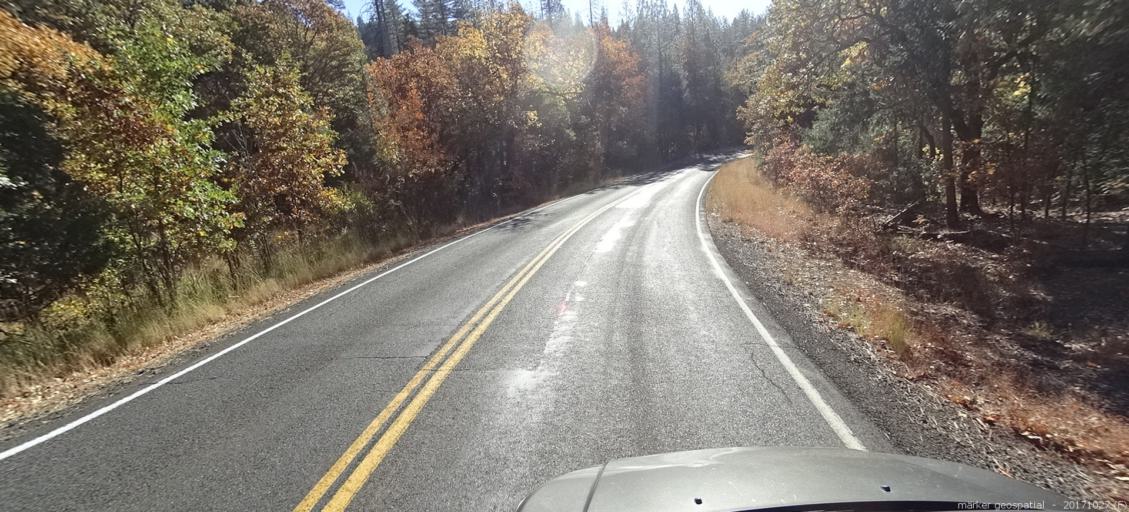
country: US
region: California
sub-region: Shasta County
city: Burney
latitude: 40.9142
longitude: -121.9088
